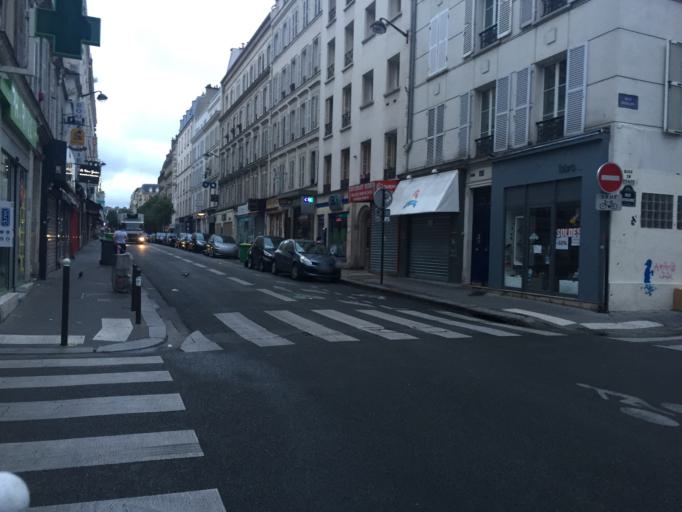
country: FR
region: Ile-de-France
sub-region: Departement des Hauts-de-Seine
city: Clichy
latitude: 48.8856
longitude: 2.3196
